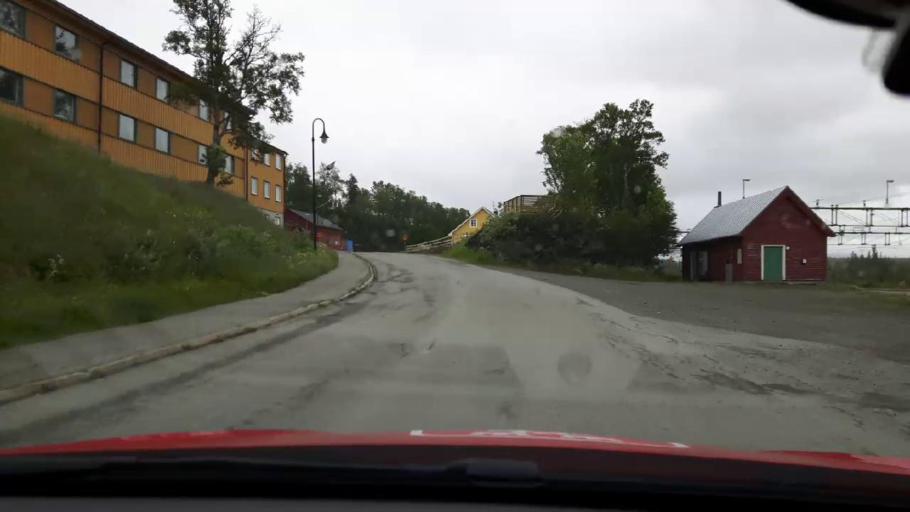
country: NO
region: Nord-Trondelag
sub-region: Meraker
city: Meraker
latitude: 63.3156
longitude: 12.1031
